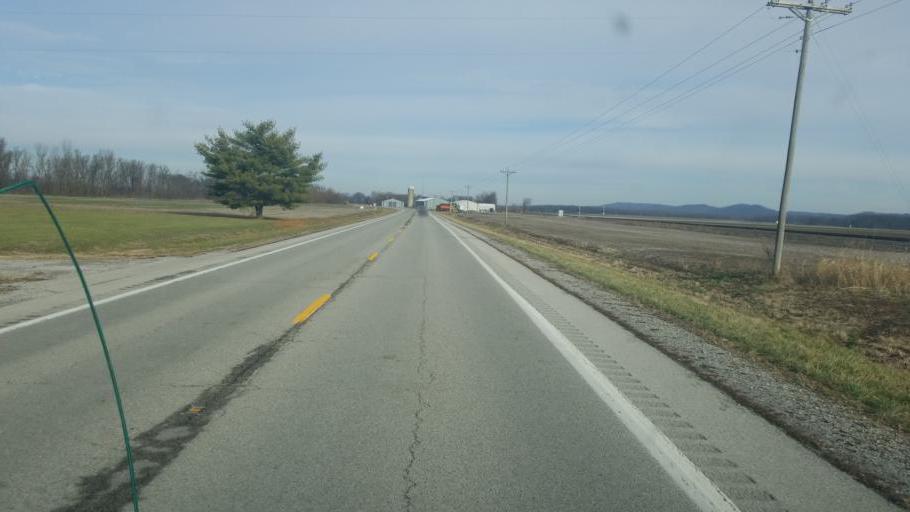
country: US
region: Missouri
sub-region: Cape Girardeau County
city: Cape Girardeau
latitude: 37.3465
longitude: -89.4028
